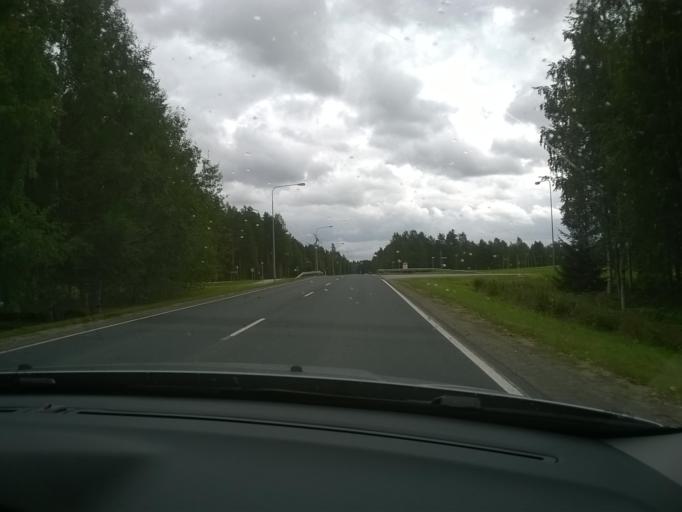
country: FI
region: Kainuu
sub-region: Kehys-Kainuu
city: Kuhmo
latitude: 64.1208
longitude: 29.5150
